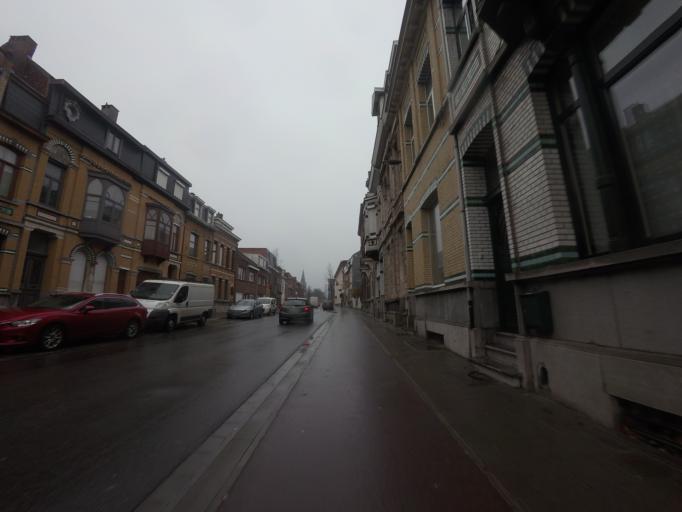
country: BE
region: Flanders
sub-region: Provincie Antwerpen
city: Hoboken
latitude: 51.1797
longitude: 4.3494
